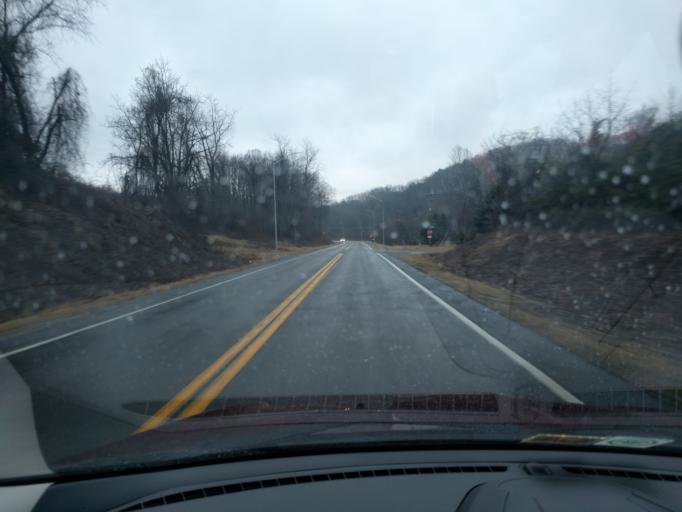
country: US
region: Virginia
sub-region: Pulaski County
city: Pulaski
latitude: 37.0378
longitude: -80.7367
